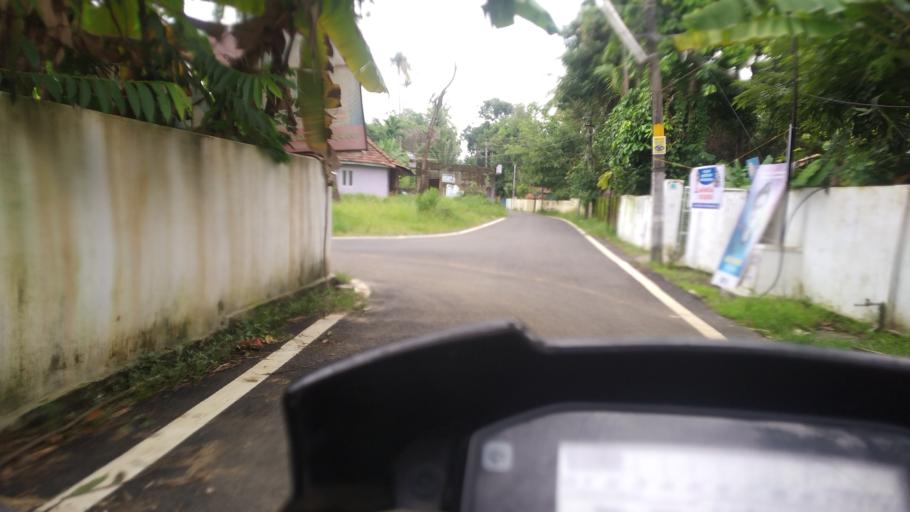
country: IN
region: Kerala
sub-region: Ernakulam
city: Elur
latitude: 10.0556
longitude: 76.2266
